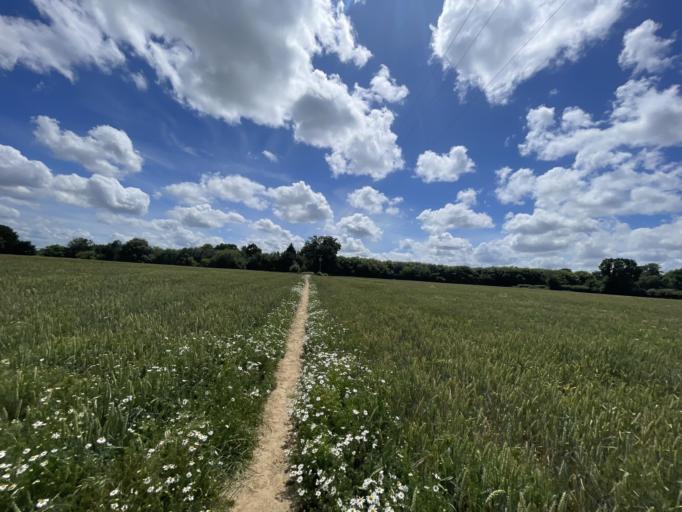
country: GB
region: England
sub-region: Kent
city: Edenbridge
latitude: 51.1645
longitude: 0.1387
